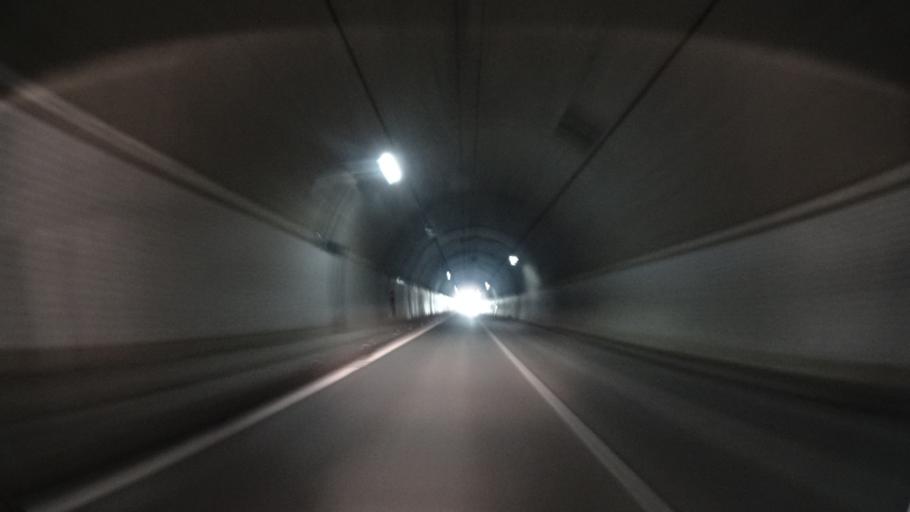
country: JP
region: Ehime
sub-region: Nishiuwa-gun
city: Ikata-cho
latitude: 33.4268
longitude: 132.2108
